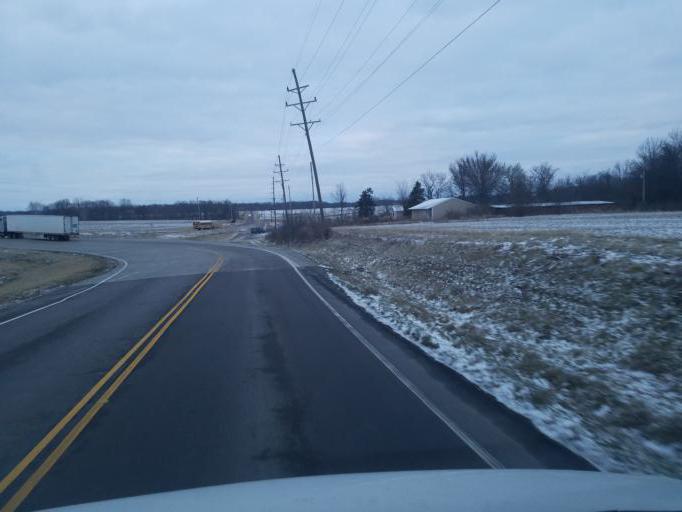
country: US
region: Missouri
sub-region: Warren County
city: Warrenton
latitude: 38.8384
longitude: -91.2271
